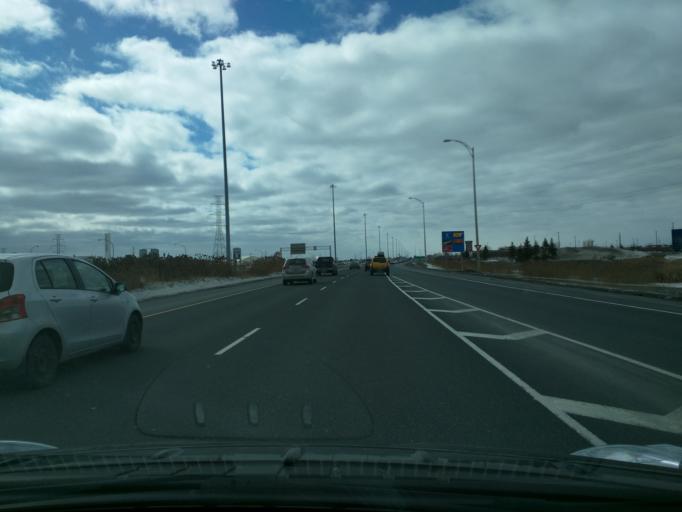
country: CA
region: Quebec
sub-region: Monteregie
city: Boucherville
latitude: 45.5707
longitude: -73.3970
